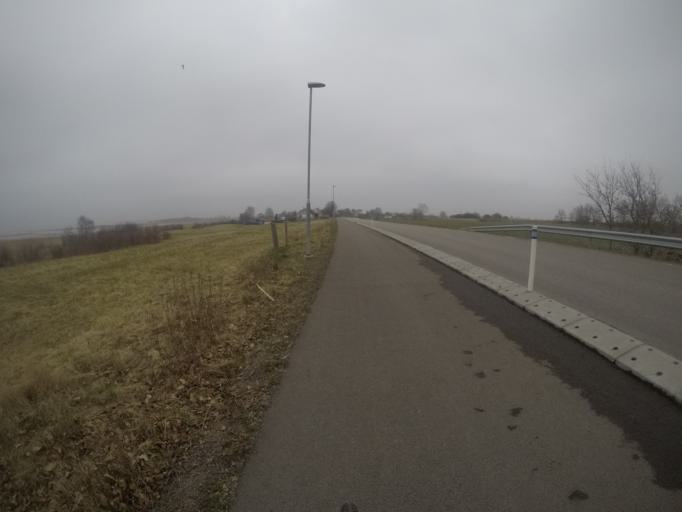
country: SE
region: Skane
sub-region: Angelholms Kommun
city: Strovelstorp
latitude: 56.2166
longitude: 12.7712
